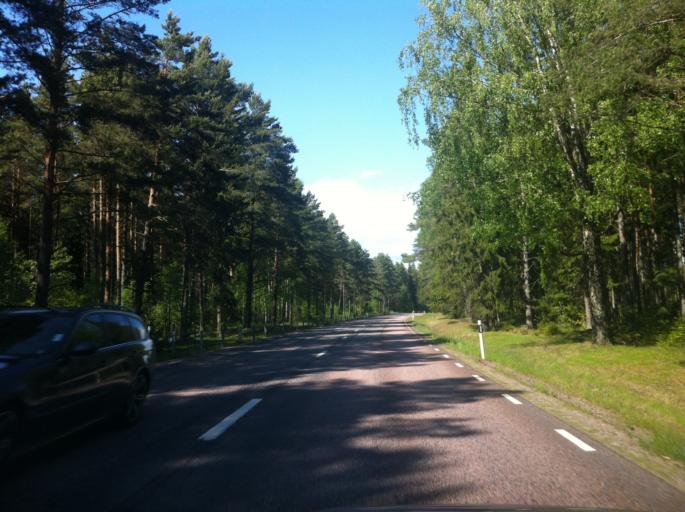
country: SE
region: Vaestra Goetaland
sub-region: Gullspangs Kommun
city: Gullspang
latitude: 59.0804
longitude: 14.1565
